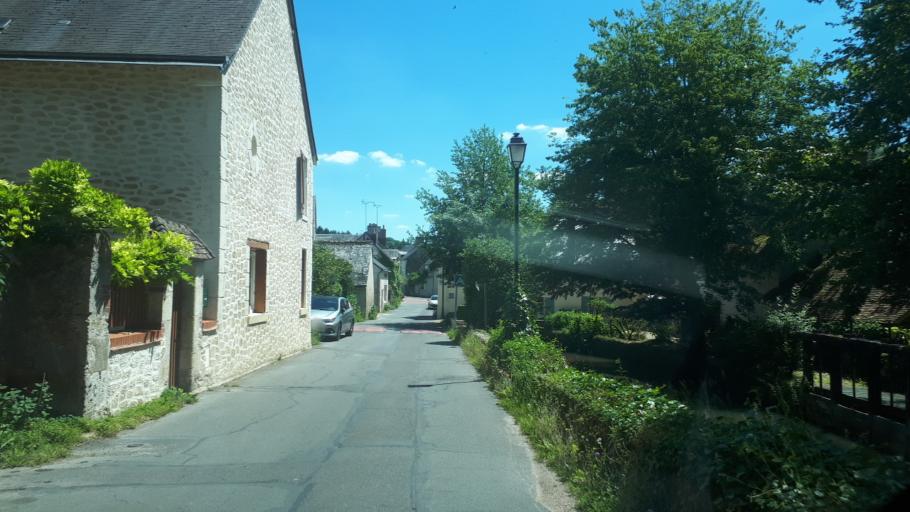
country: FR
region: Centre
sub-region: Departement du Loir-et-Cher
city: Saint-Sulpice-de-Pommeray
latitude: 47.5792
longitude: 1.2153
